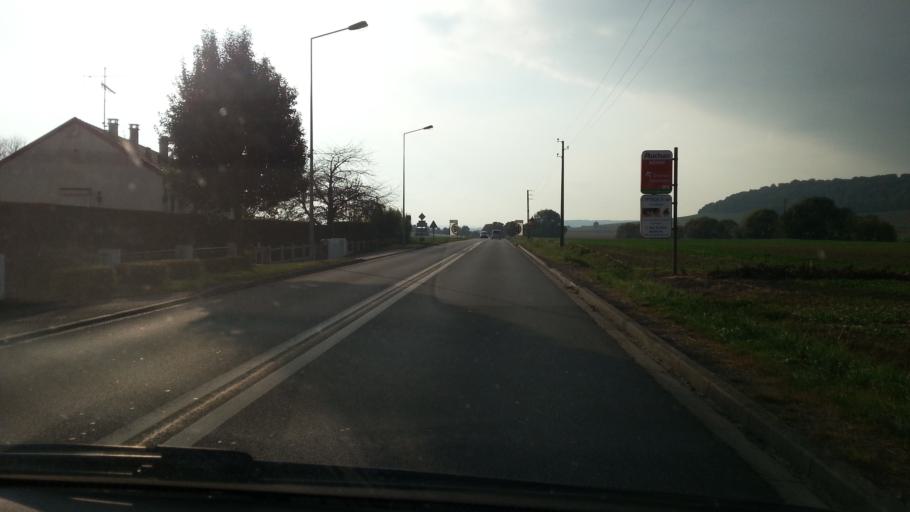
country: FR
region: Picardie
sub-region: Departement de l'Oise
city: Noyon
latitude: 49.5810
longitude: 3.0529
